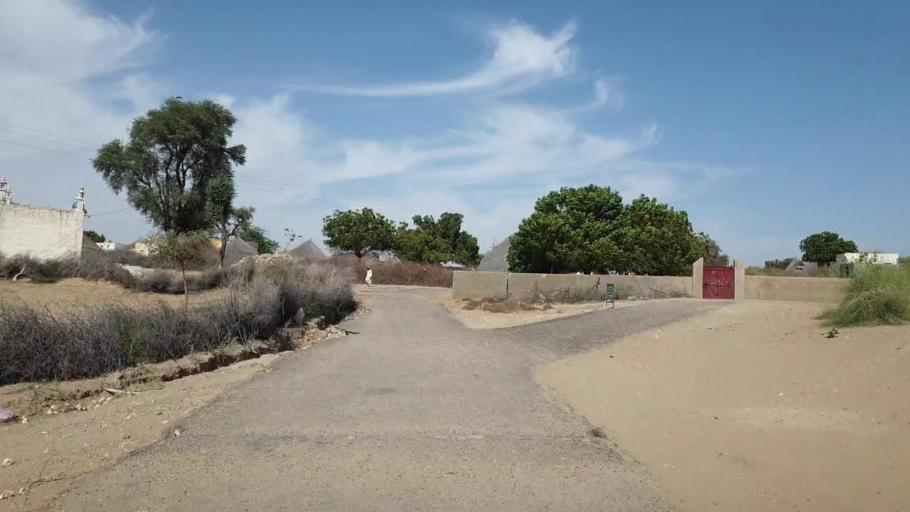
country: PK
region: Sindh
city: Umarkot
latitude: 25.1644
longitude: 70.0074
